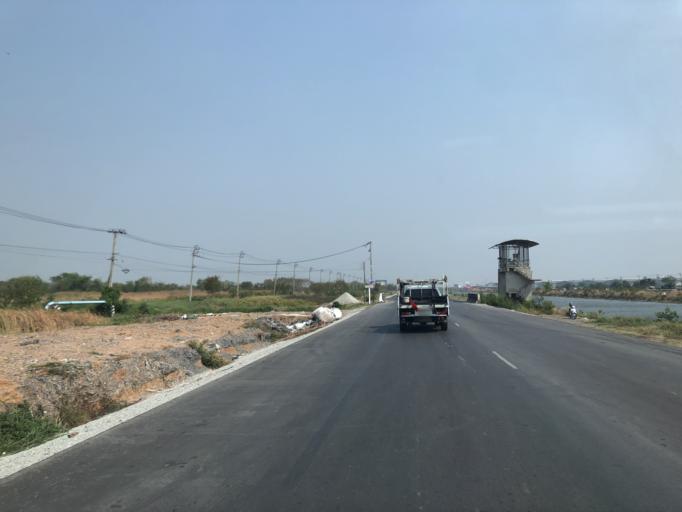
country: TH
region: Samut Prakan
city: Bang Bo District
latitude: 13.5472
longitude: 100.7518
